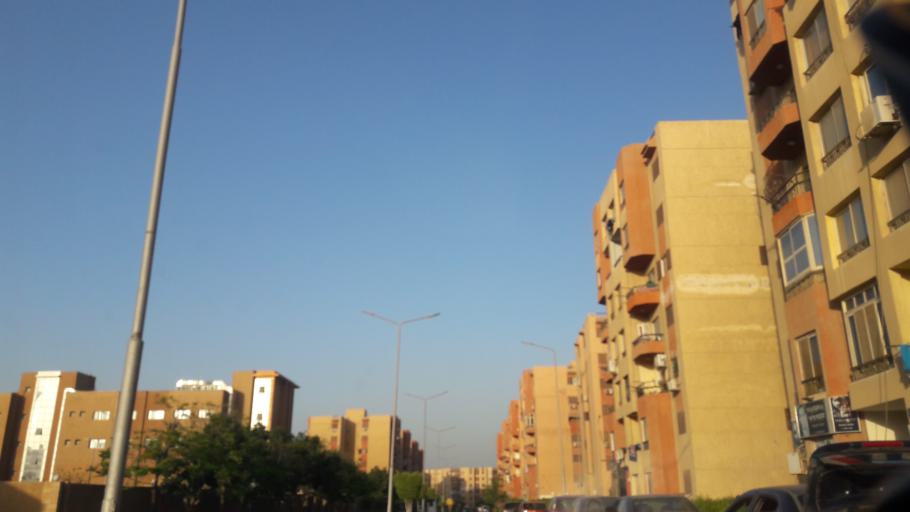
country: EG
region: Al Jizah
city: Madinat Sittah Uktubar
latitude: 29.9552
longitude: 31.0418
